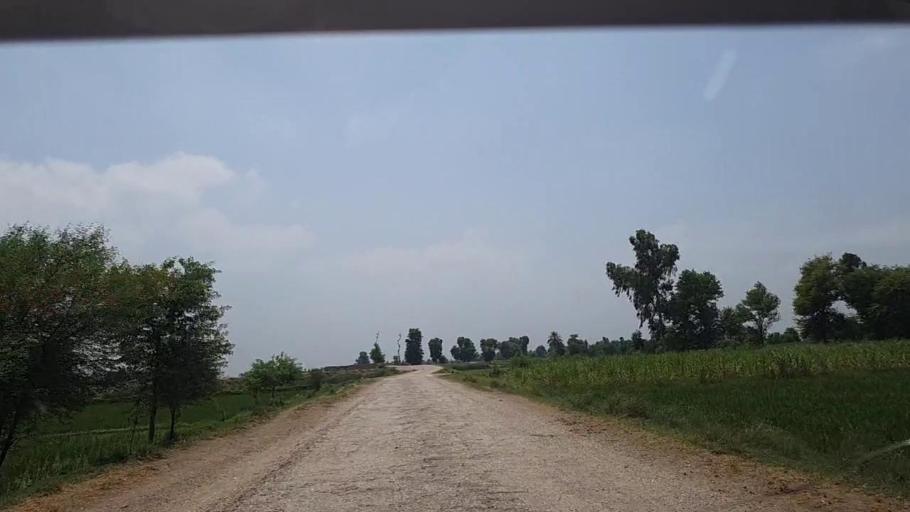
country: PK
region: Sindh
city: Khanpur
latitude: 27.9090
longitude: 69.3929
